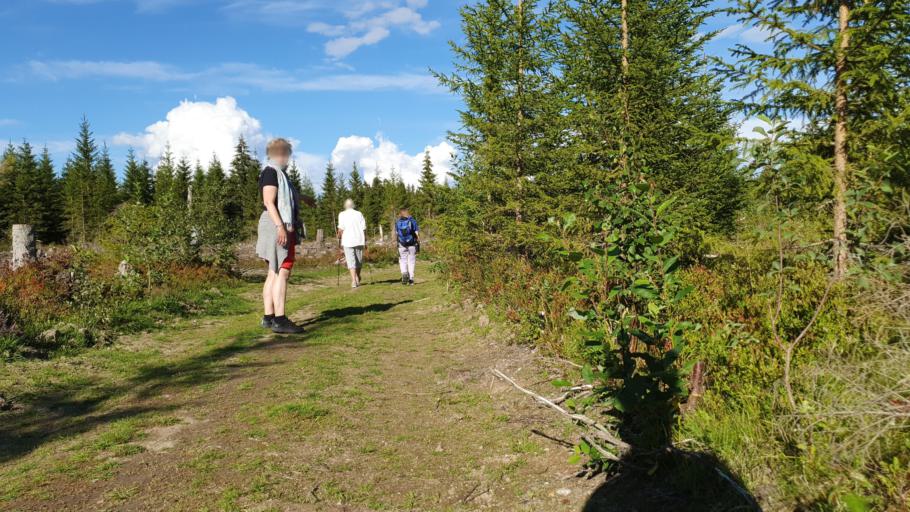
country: NO
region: Nord-Trondelag
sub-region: Levanger
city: Levanger
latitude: 63.6930
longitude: 11.2759
